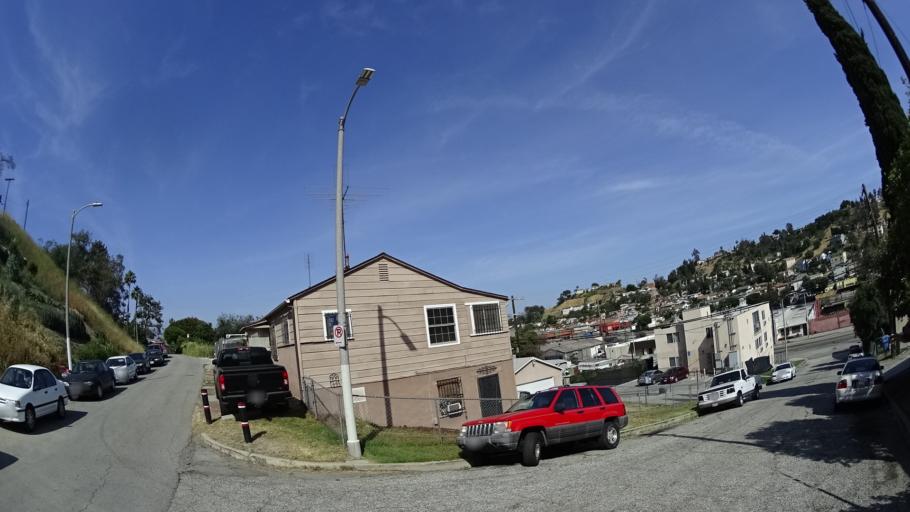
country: US
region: California
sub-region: Los Angeles County
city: Belvedere
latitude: 34.0709
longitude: -118.1768
